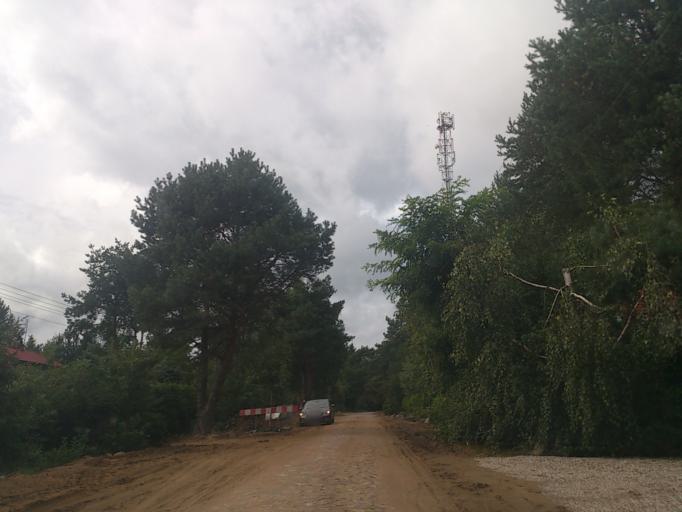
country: PL
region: Greater Poland Voivodeship
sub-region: Powiat poznanski
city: Kobylnica
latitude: 52.5175
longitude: 17.1342
